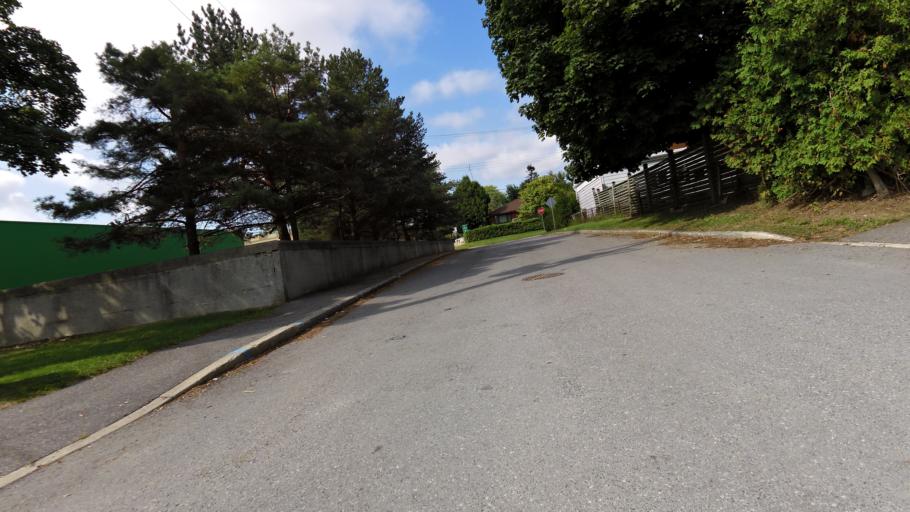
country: CA
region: Ontario
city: Ottawa
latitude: 45.3870
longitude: -75.7387
